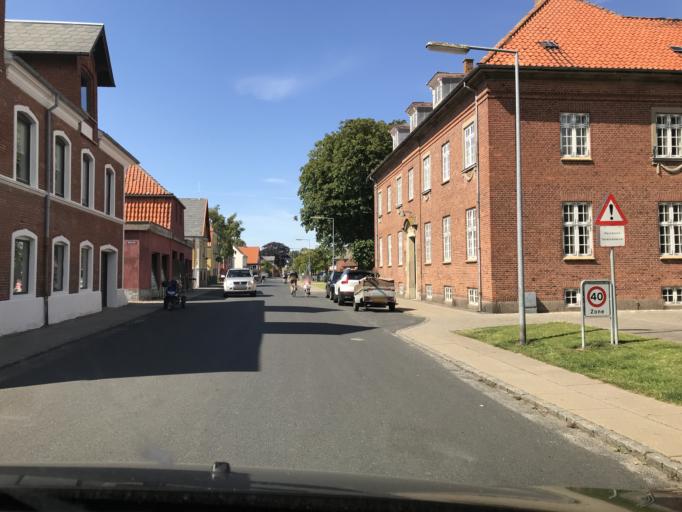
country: DK
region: South Denmark
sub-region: AEro Kommune
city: Marstal
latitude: 54.8546
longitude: 10.5212
